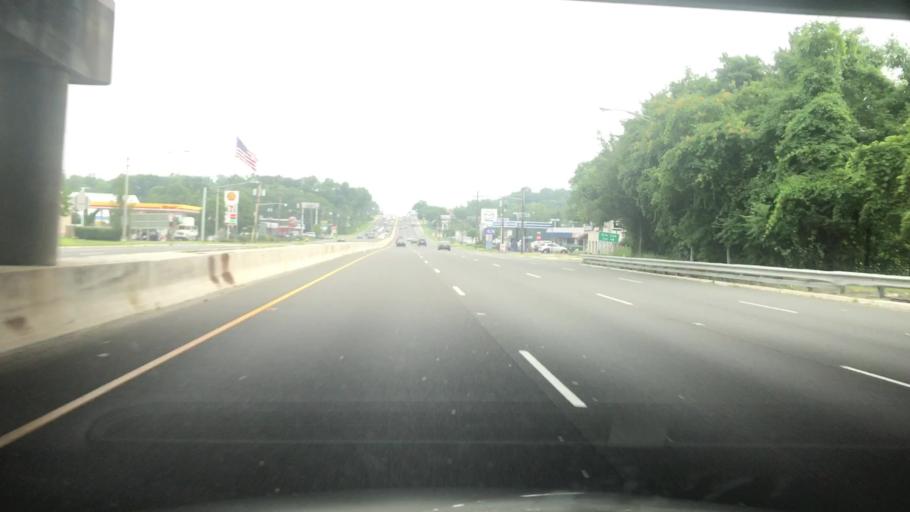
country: US
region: New Jersey
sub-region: Passaic County
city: Wayne
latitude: 40.9246
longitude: -74.2682
